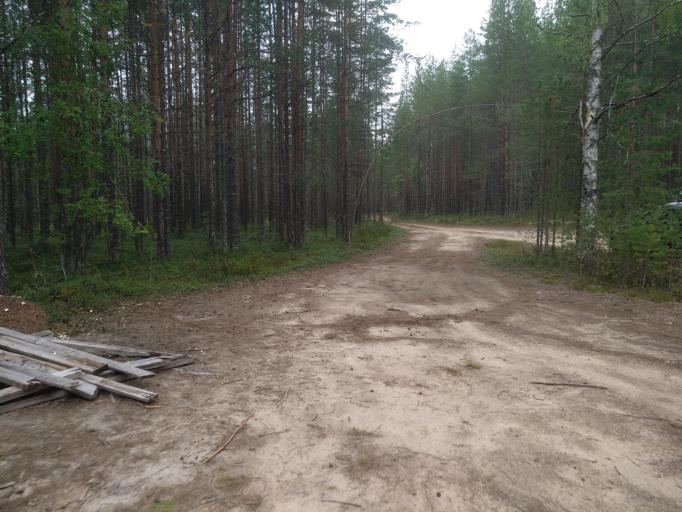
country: RU
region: Republic of Karelia
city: Borovoy
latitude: 64.1094
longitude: 33.1896
